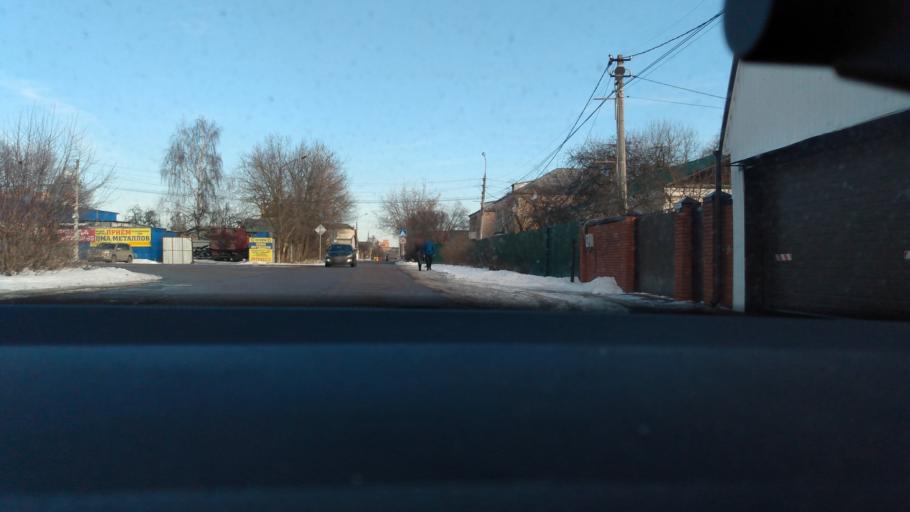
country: RU
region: Moskovskaya
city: Ramenskoye
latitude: 55.5644
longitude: 38.2097
